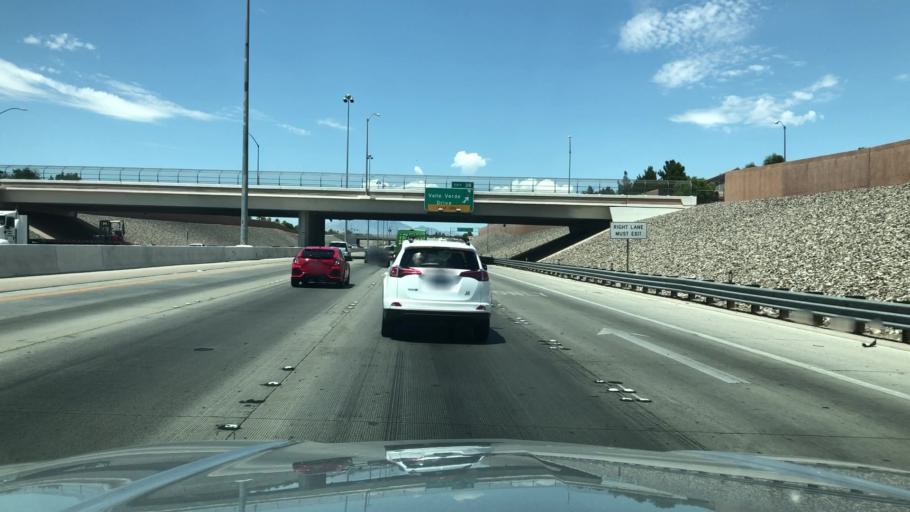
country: US
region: Nevada
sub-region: Clark County
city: Whitney
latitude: 36.0285
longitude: -115.0549
